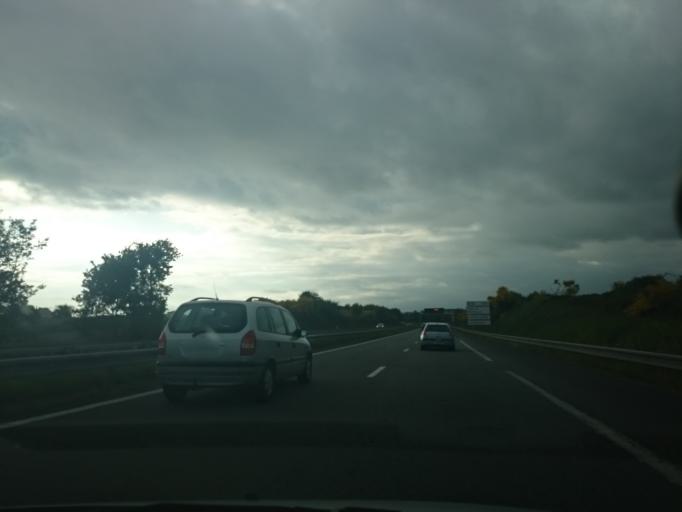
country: FR
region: Brittany
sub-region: Departement du Morbihan
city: Theix
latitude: 47.6251
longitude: -2.6326
